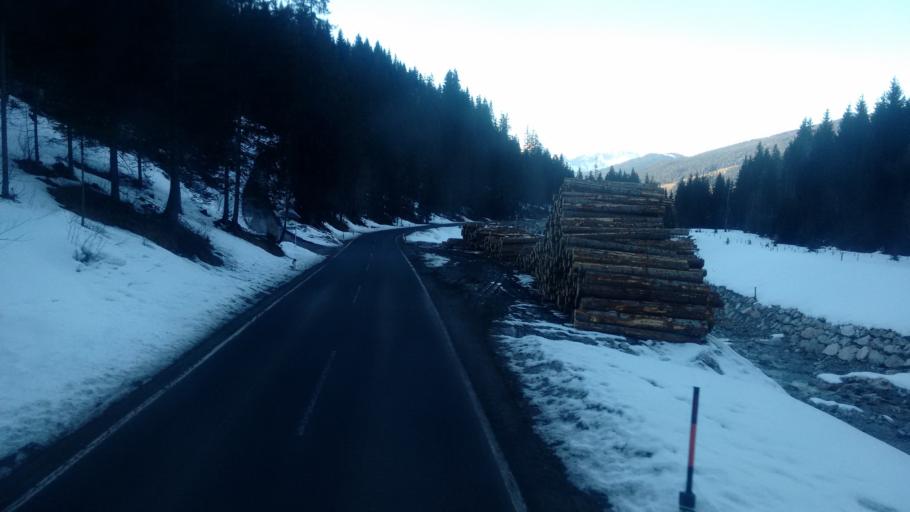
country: AT
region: Salzburg
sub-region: Politischer Bezirk Sankt Johann im Pongau
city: Altenmarkt im Pongau
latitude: 47.3477
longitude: 13.4302
